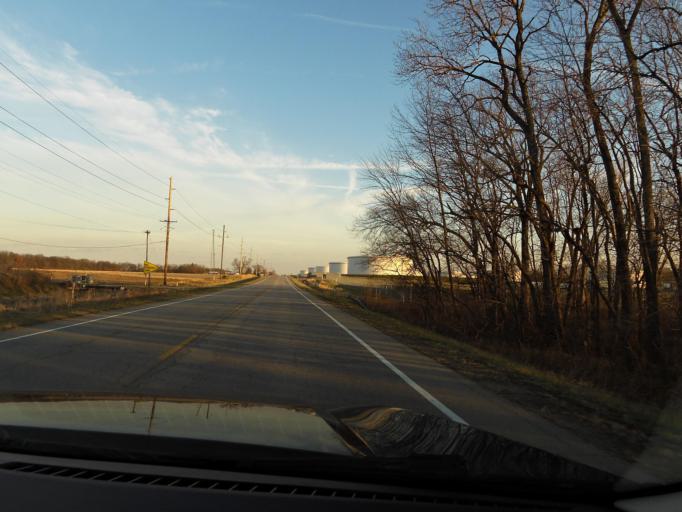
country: US
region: Illinois
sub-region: Marion County
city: Odin
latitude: 38.7753
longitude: -89.0865
